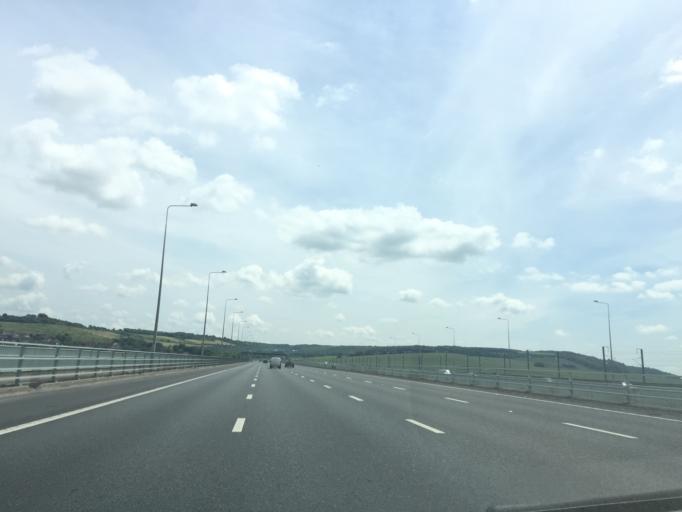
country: GB
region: England
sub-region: Medway
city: Cuxton
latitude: 51.3782
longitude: 0.4738
